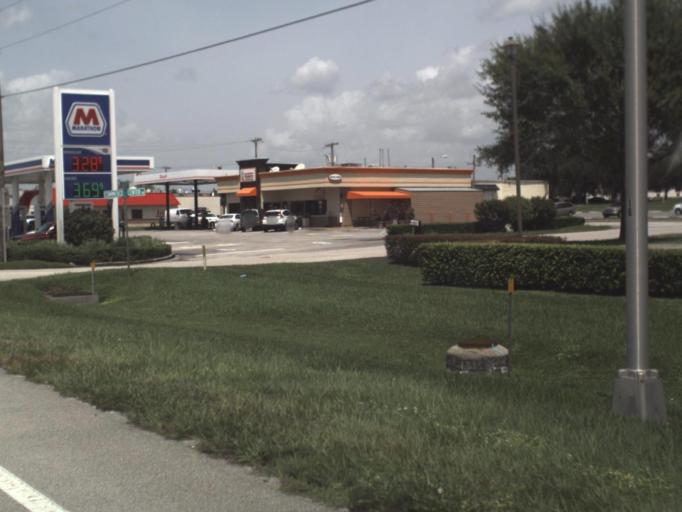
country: US
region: Florida
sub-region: Highlands County
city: Sebring
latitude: 27.4673
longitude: -81.4374
